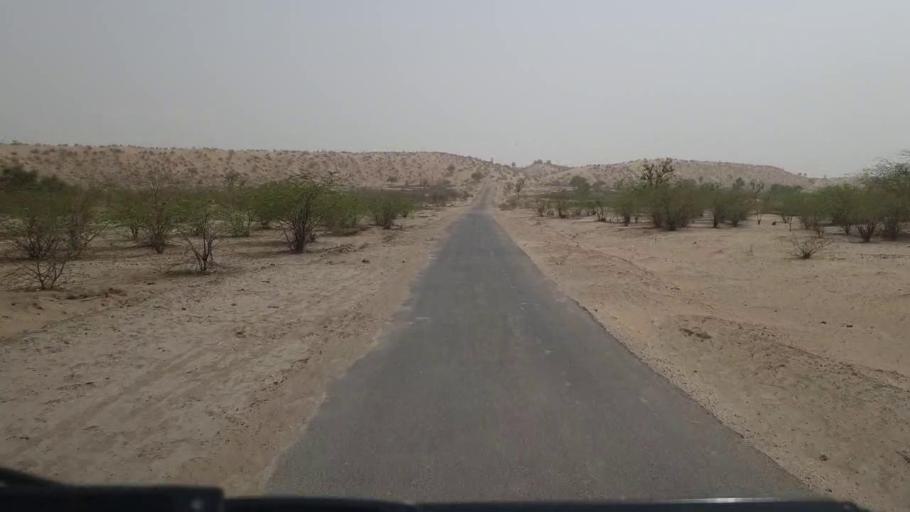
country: PK
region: Sindh
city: Islamkot
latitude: 25.2646
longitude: 70.6488
